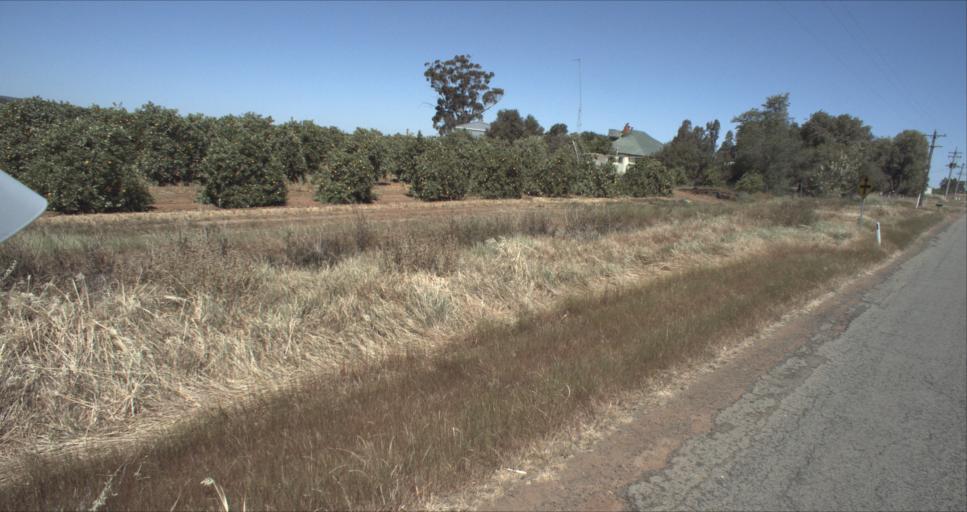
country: AU
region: New South Wales
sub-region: Leeton
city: Leeton
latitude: -34.4789
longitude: 146.4155
